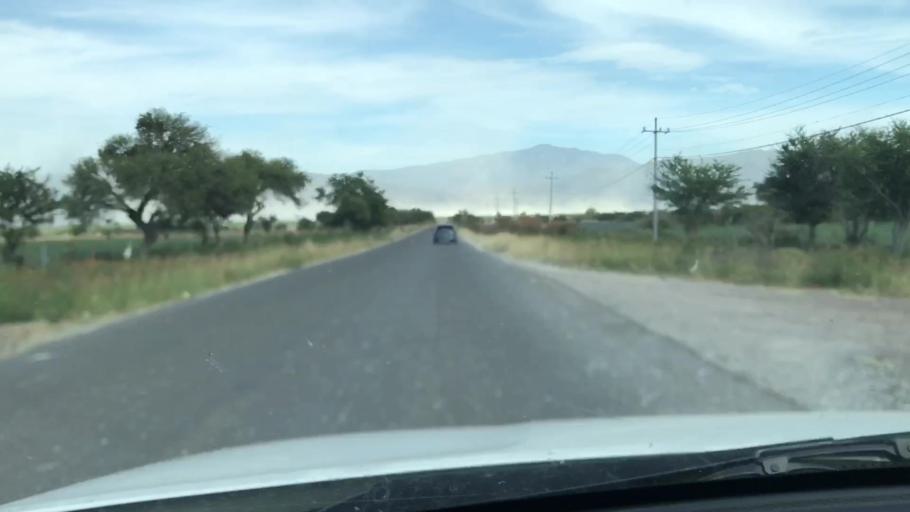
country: MX
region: Jalisco
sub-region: Zacoalco de Torres
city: Barranca de Otates (Barranca de Otatan)
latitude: 20.2824
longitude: -103.6188
